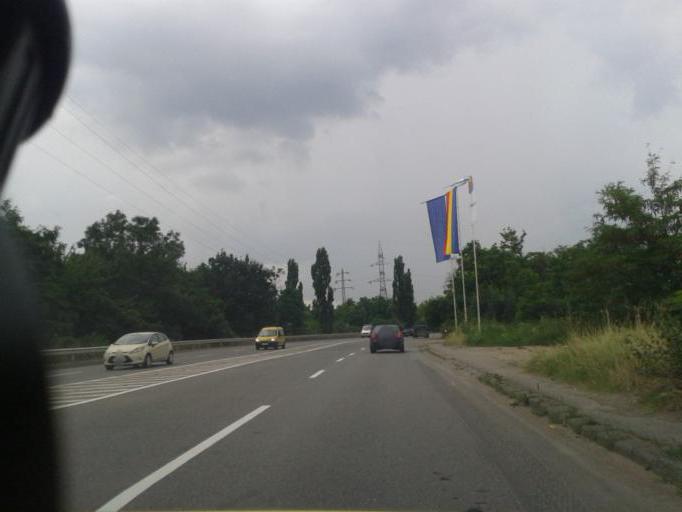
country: RO
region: Prahova
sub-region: Comuna Bucov
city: Bucov
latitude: 44.9637
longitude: 26.0608
